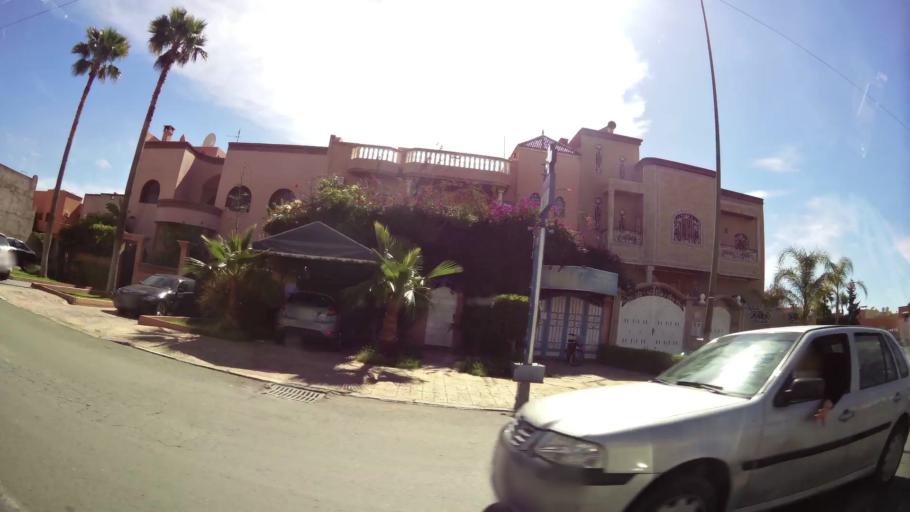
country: MA
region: Marrakech-Tensift-Al Haouz
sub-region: Marrakech
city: Marrakesh
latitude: 31.6497
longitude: -8.0485
